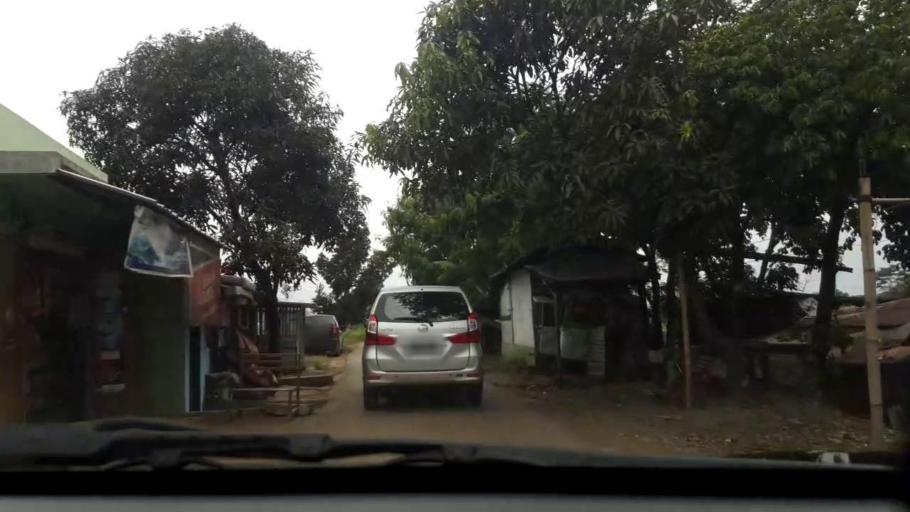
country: ID
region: West Java
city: Cileunyi
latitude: -6.9496
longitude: 107.7132
